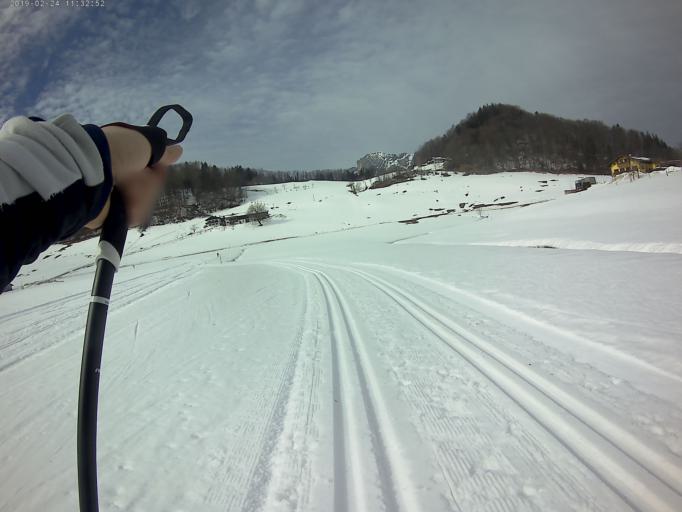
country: AT
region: Salzburg
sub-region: Politischer Bezirk Hallein
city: Hallein
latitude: 47.6767
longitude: 13.0690
